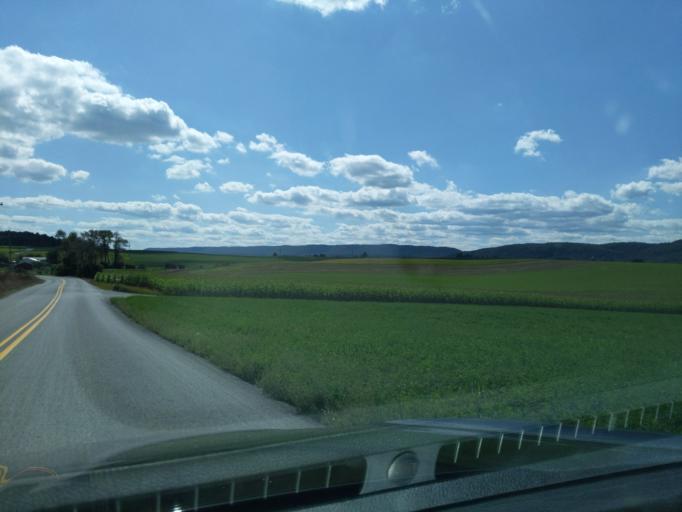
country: US
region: Pennsylvania
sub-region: Blair County
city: Tyrone
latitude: 40.6419
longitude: -78.2201
